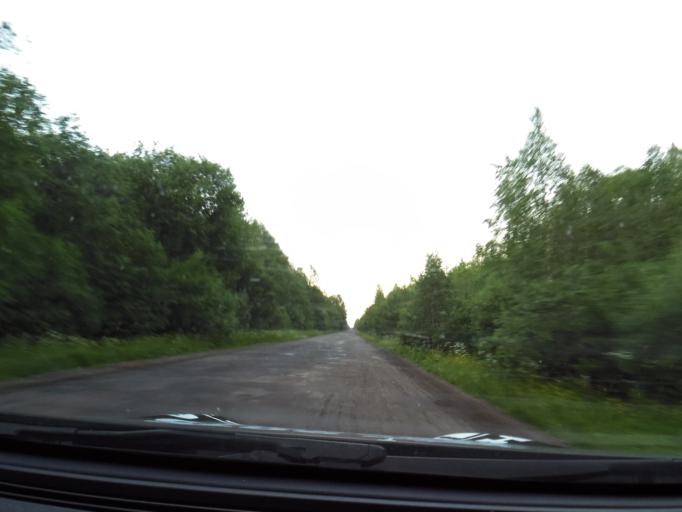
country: RU
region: Leningrad
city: Voznesen'ye
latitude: 60.8328
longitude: 35.6795
